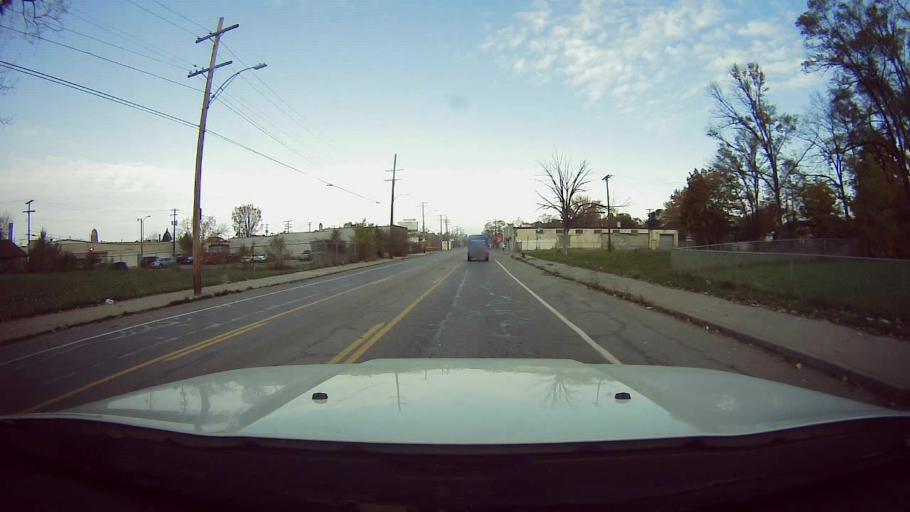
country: US
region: Michigan
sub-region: Wayne County
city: Dearborn
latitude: 42.3701
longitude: -83.1778
